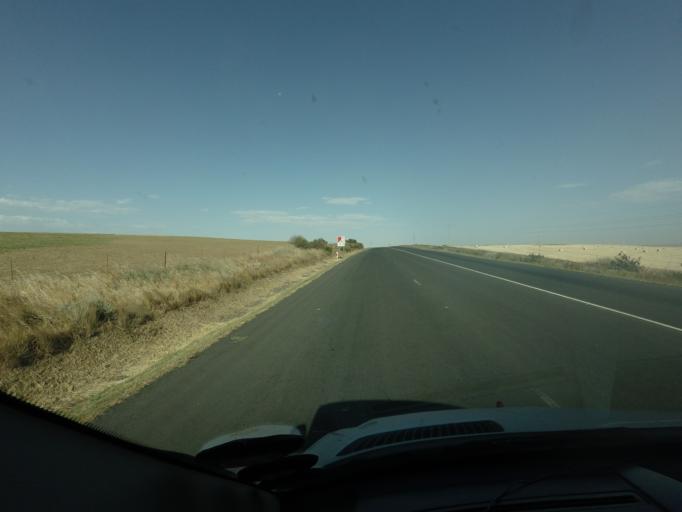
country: ZA
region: Western Cape
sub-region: Cape Winelands District Municipality
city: Ashton
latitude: -34.1581
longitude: 19.9574
